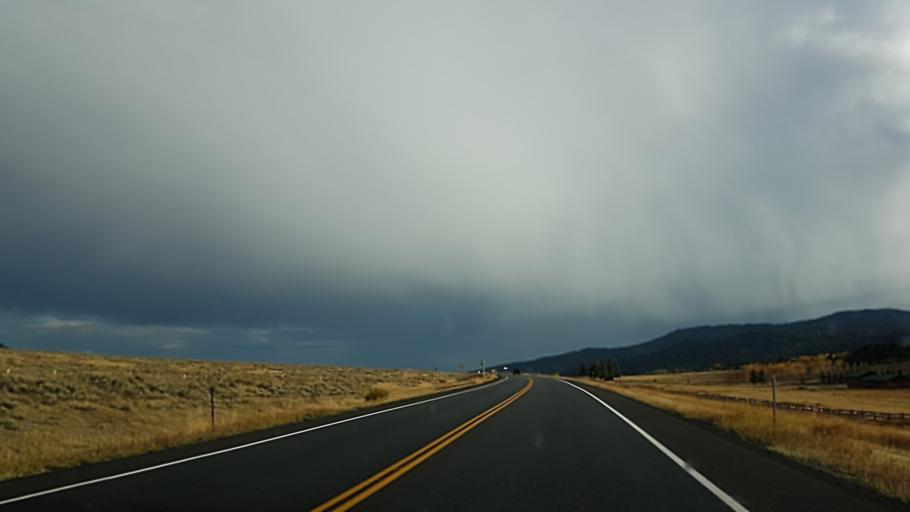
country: US
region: Montana
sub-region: Gallatin County
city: West Yellowstone
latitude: 44.7137
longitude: -111.4707
